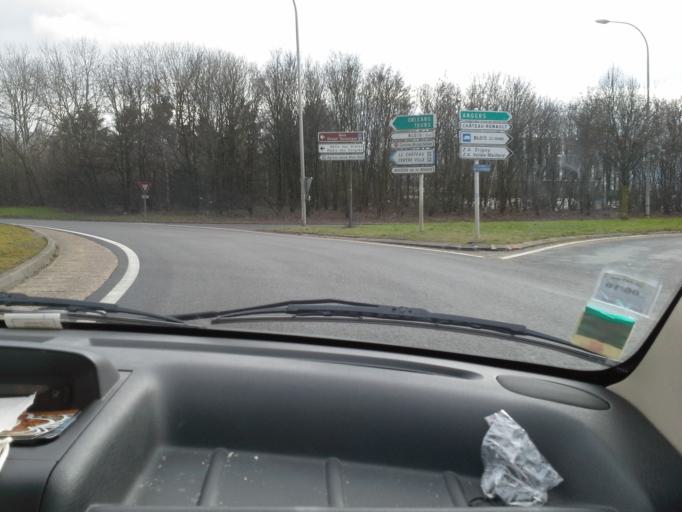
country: FR
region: Centre
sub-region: Departement du Loir-et-Cher
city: Villebarou
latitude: 47.6104
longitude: 1.3381
